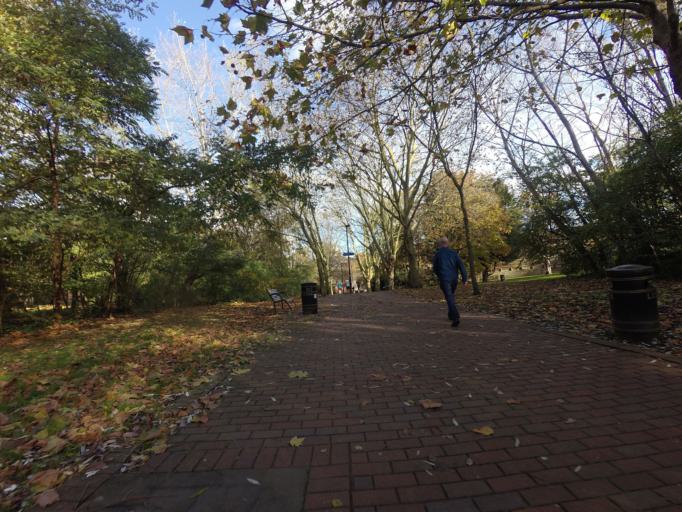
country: GB
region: England
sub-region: Greater London
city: Bethnal Green
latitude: 51.5078
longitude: -0.0566
